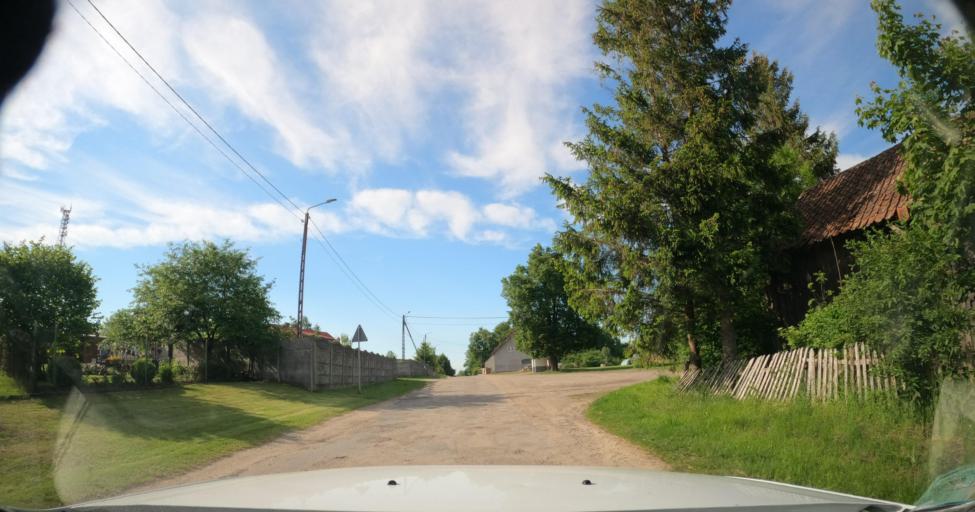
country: PL
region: Warmian-Masurian Voivodeship
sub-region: Powiat ostrodzki
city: Morag
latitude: 54.0636
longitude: 19.8895
